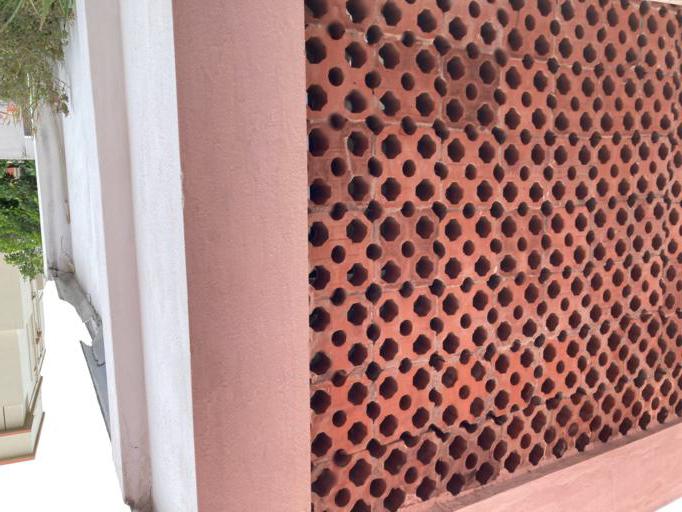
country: IN
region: Andhra Pradesh
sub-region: West Godavari
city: Eluru
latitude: 16.7149
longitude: 81.1009
